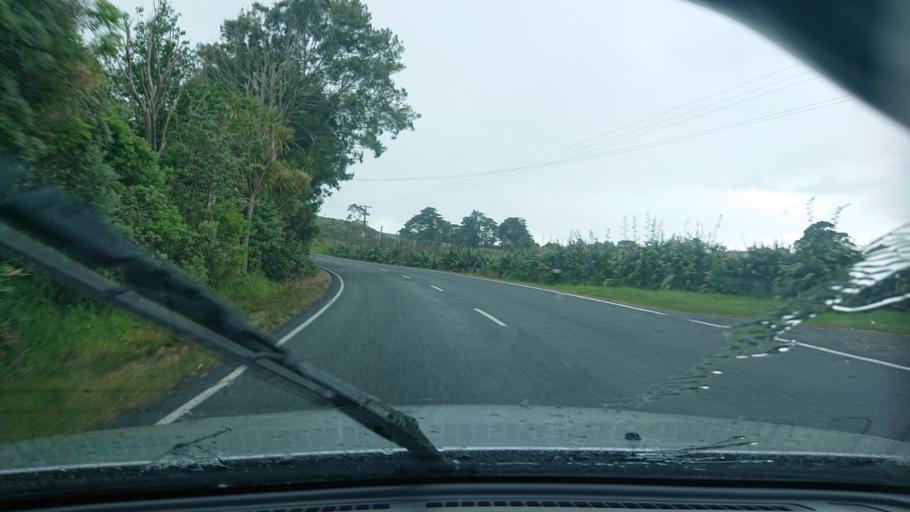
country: NZ
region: Auckland
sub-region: Auckland
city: Wellsford
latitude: -36.3302
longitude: 174.4058
